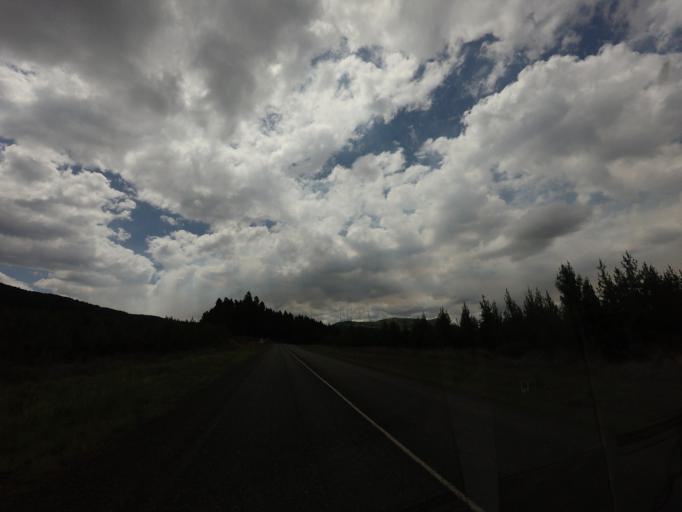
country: ZA
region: Mpumalanga
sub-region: Ehlanzeni District
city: Graksop
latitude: -24.9717
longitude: 30.8061
